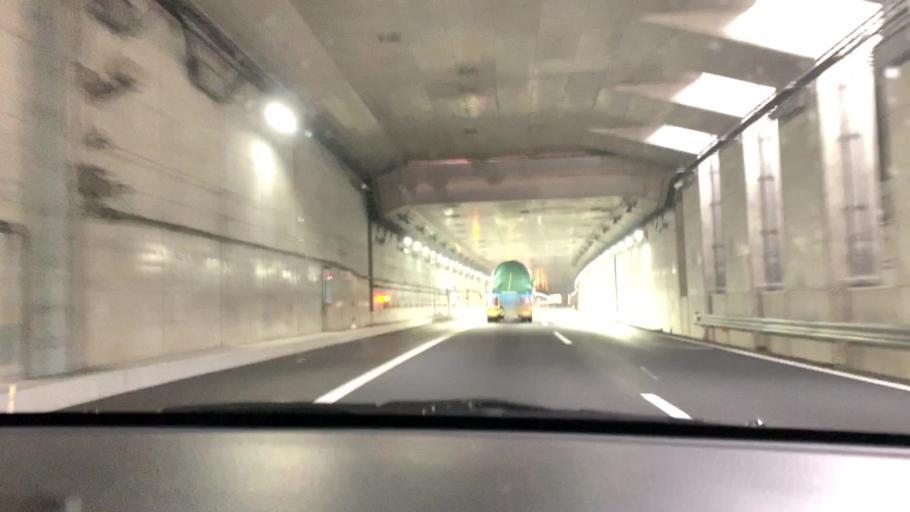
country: JP
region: Tokyo
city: Urayasu
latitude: 35.7055
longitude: 139.9277
